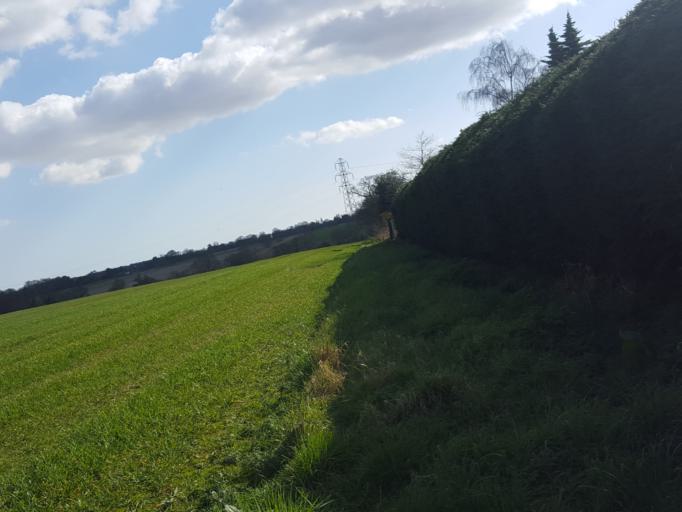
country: GB
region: England
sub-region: Essex
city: Little Clacton
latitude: 51.8724
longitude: 1.1147
